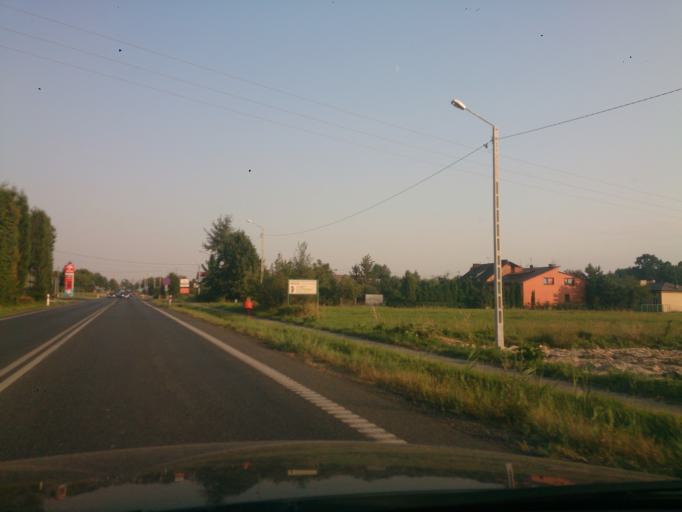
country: PL
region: Subcarpathian Voivodeship
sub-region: Powiat kolbuszowski
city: Kolbuszowa
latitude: 50.2591
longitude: 21.7645
